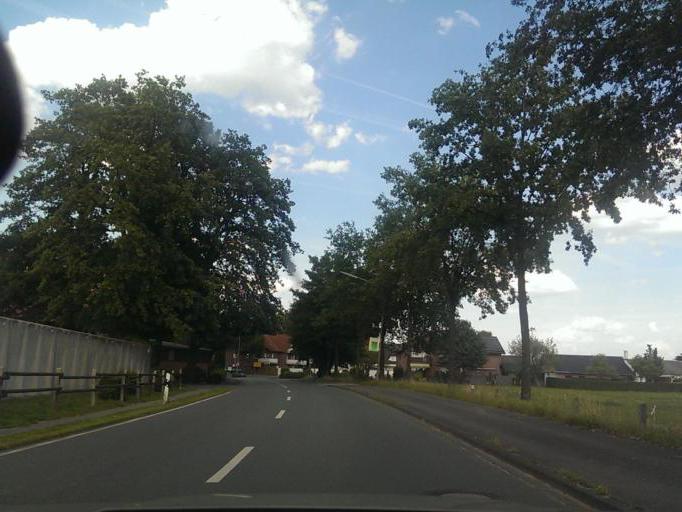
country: DE
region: North Rhine-Westphalia
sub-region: Regierungsbezirk Detmold
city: Delbruck
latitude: 51.7432
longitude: 8.5896
